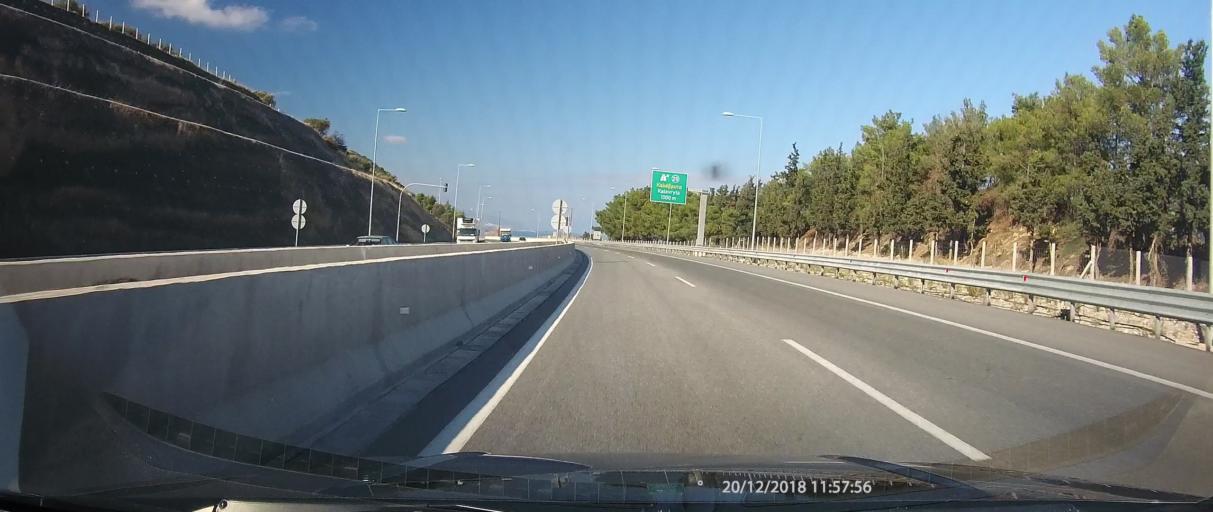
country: GR
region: West Greece
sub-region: Nomos Achaias
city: Akrata
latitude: 38.1730
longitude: 22.2584
